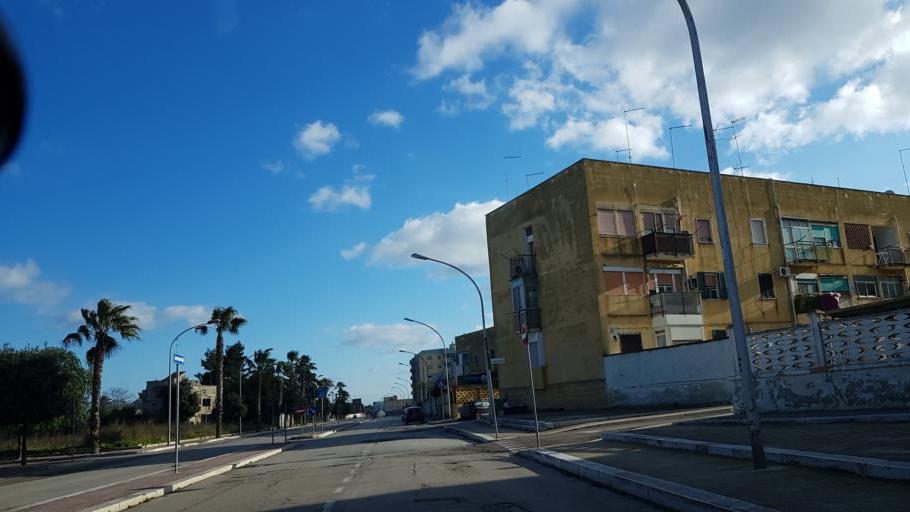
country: IT
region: Apulia
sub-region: Provincia di Brindisi
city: Brindisi
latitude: 40.6504
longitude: 17.9177
